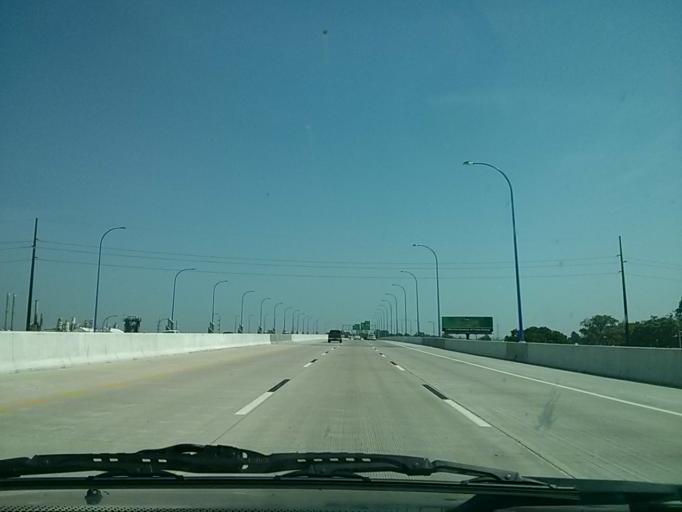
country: US
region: Oklahoma
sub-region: Tulsa County
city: Tulsa
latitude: 36.1365
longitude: -96.0079
